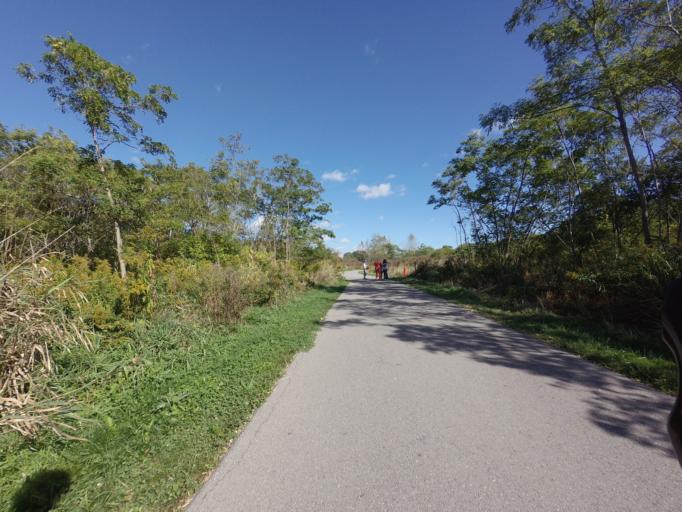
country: CA
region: Ontario
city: Ajax
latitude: 43.8512
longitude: -78.9667
